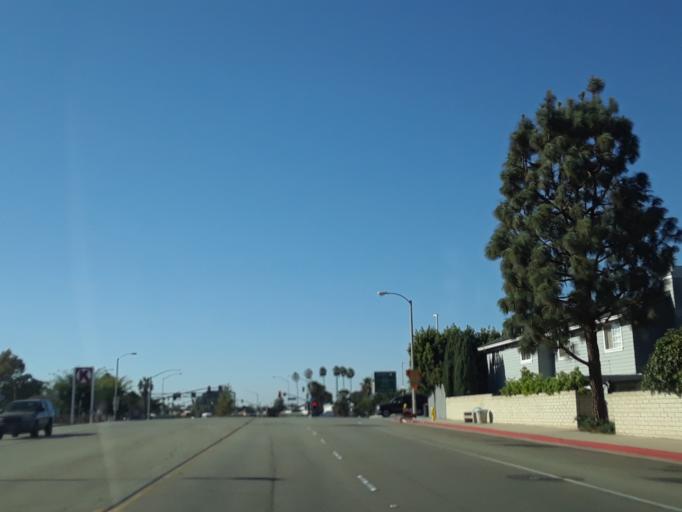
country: US
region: California
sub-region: Orange County
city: Costa Mesa
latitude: 33.6620
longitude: -117.8957
